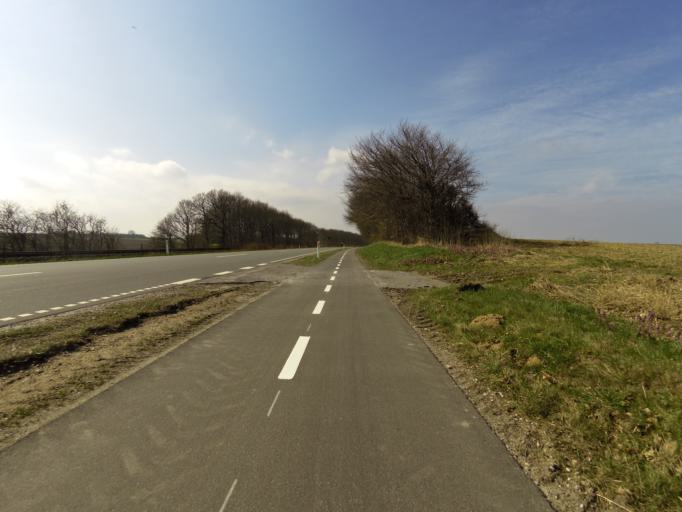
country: DK
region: Central Jutland
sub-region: Struer Kommune
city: Struer
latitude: 56.4654
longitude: 8.6773
